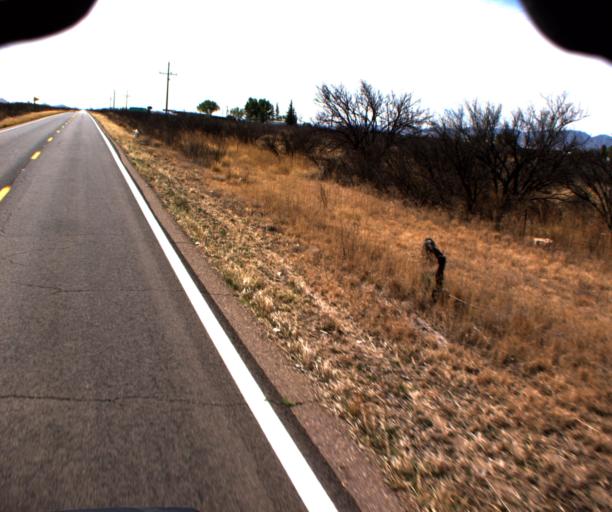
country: US
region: Arizona
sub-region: Cochise County
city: Willcox
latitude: 32.0095
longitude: -109.8657
